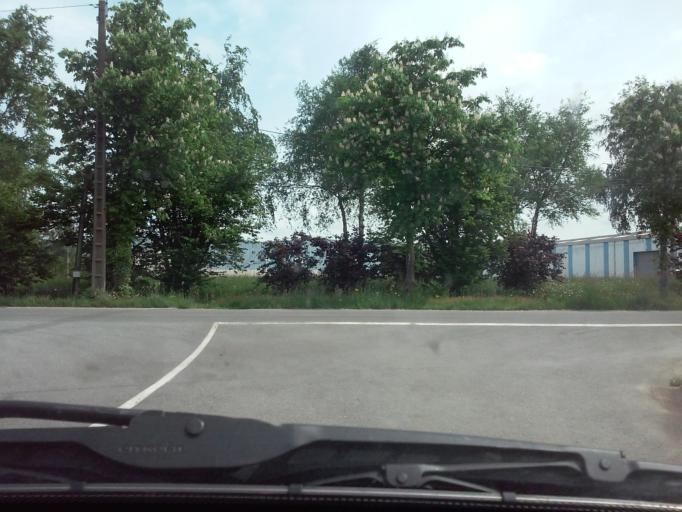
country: FR
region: Brittany
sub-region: Departement d'Ille-et-Vilaine
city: Beauce
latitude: 48.3308
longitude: -1.1638
